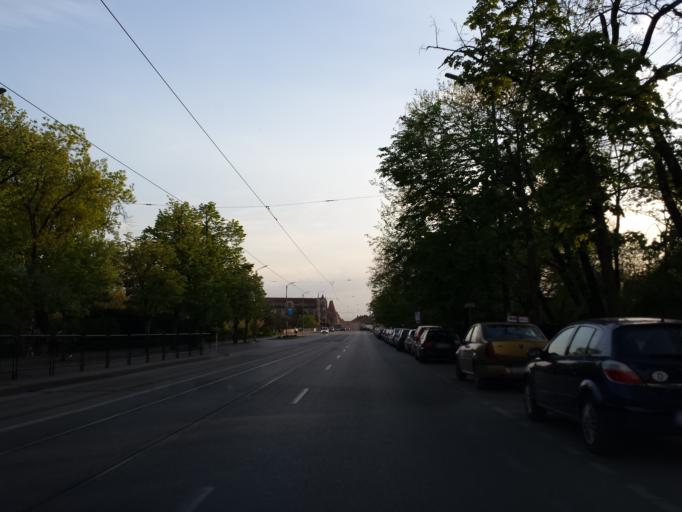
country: RO
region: Timis
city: Timisoara
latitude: 45.7511
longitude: 21.2233
